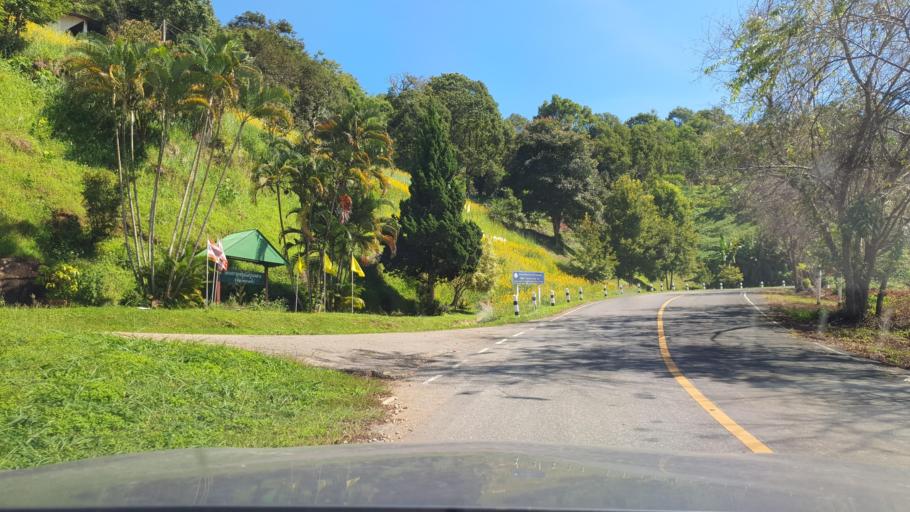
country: TH
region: Chiang Mai
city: Phrao
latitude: 19.3331
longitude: 99.3136
